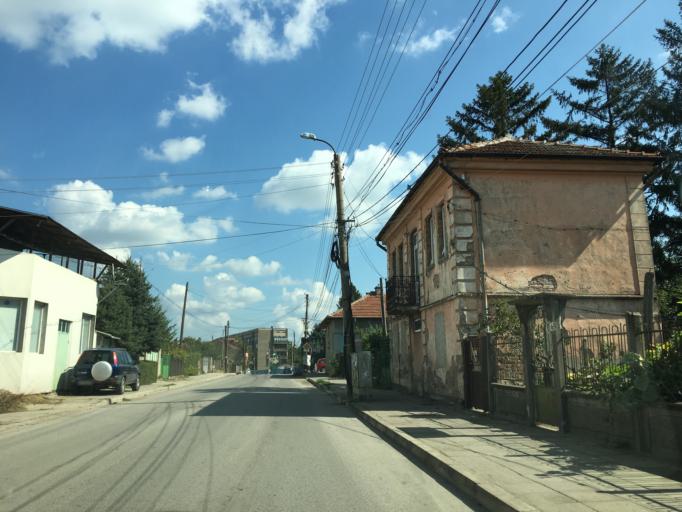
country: BG
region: Montana
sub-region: Obshtina Lom
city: Lom
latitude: 43.8298
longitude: 23.2239
